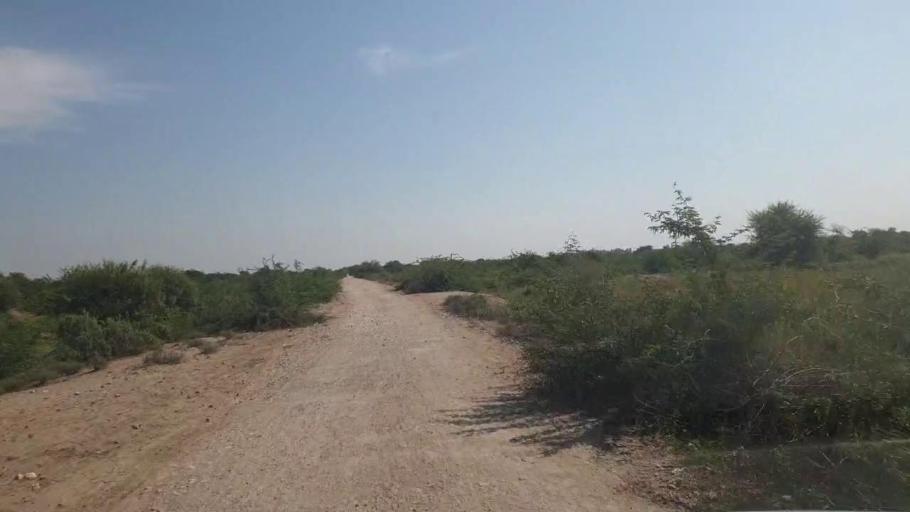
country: PK
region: Sindh
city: Digri
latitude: 24.9548
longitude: 69.1402
